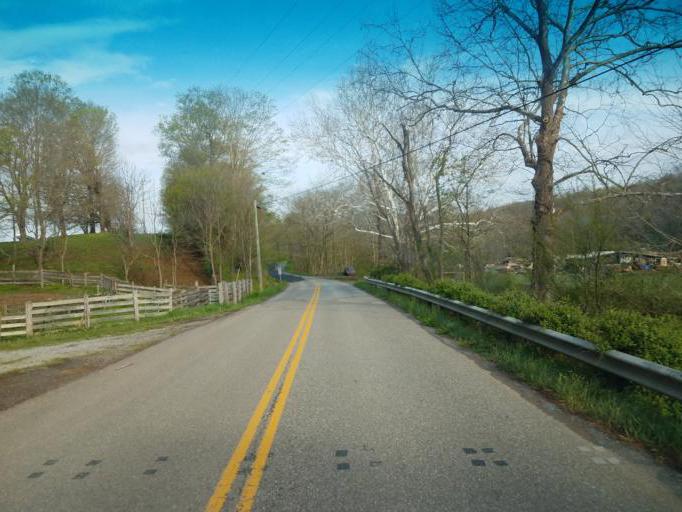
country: US
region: Virginia
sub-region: Smyth County
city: Atkins
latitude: 36.7745
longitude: -81.4210
